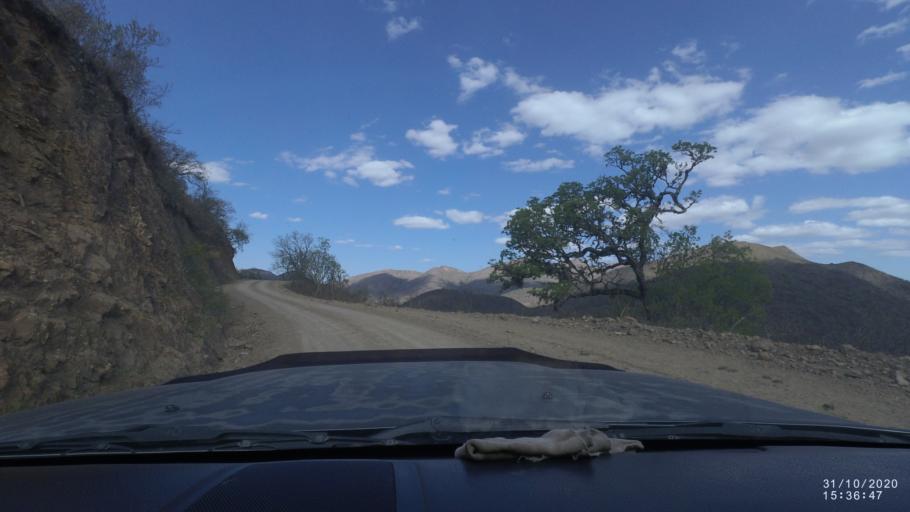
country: BO
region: Chuquisaca
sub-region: Provincia Zudanez
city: Mojocoya
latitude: -18.3406
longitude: -64.7519
